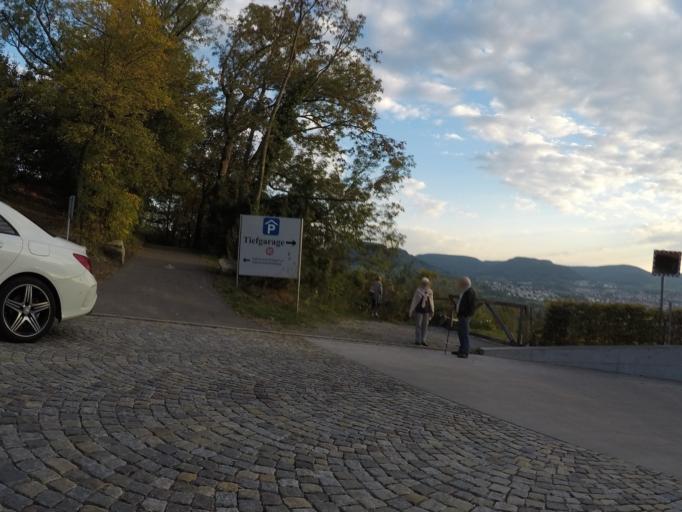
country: DE
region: Baden-Wuerttemberg
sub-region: Tuebingen Region
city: Eningen unter Achalm
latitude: 48.4911
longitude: 9.2403
